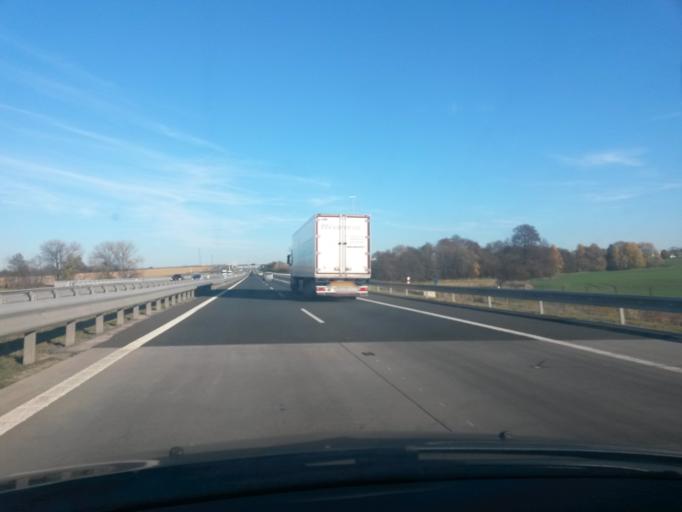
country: CZ
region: Central Bohemia
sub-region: Okres Praha-Zapad
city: Pruhonice
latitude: 49.9730
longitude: 14.5771
